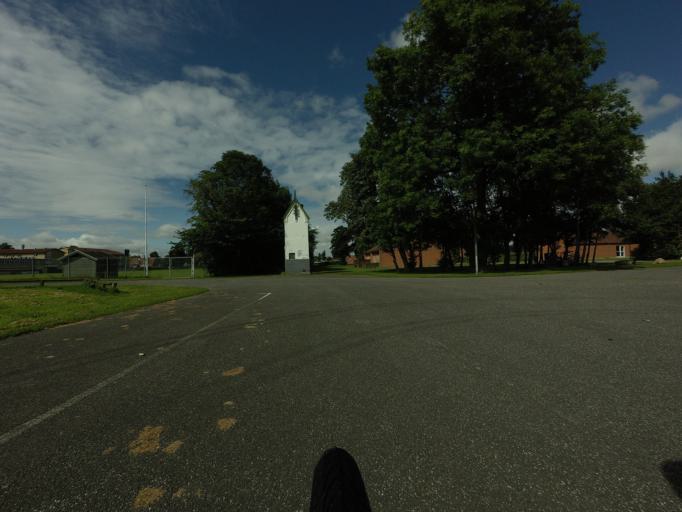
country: DK
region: Central Jutland
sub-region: Norddjurs Kommune
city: Allingabro
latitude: 56.4658
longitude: 10.3242
